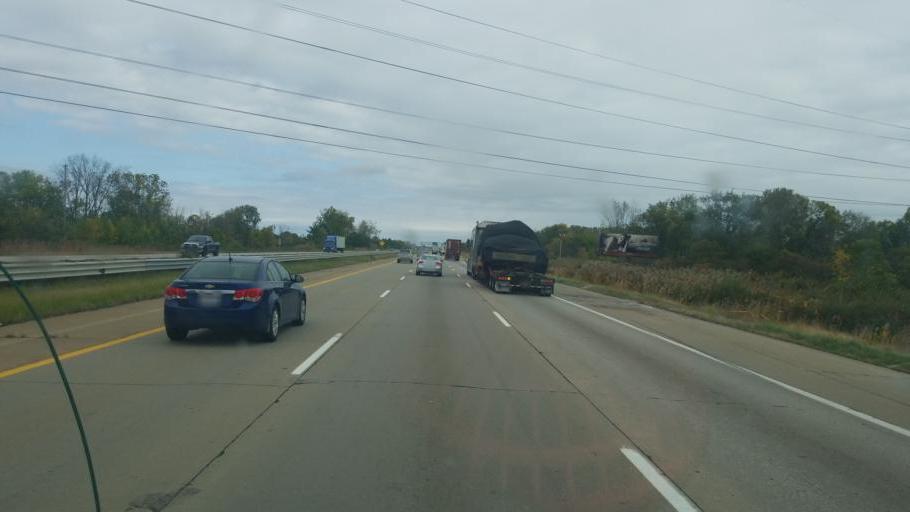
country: US
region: Michigan
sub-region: Monroe County
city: Luna Pier
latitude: 41.7859
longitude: -83.4690
